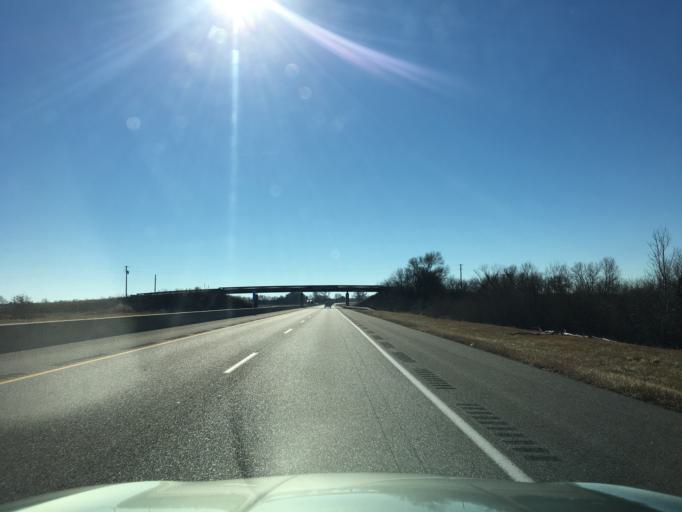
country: US
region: Kansas
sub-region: Sumner County
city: Belle Plaine
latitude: 37.4230
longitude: -97.3213
